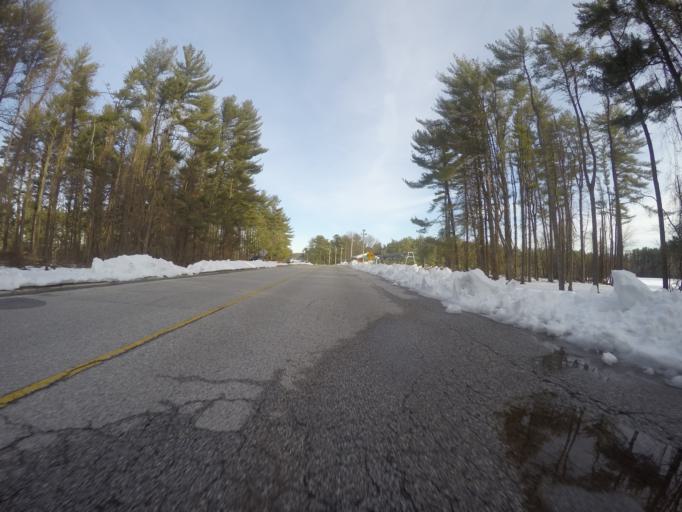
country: US
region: Maryland
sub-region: Baltimore County
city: Hampton
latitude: 39.4455
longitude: -76.5851
